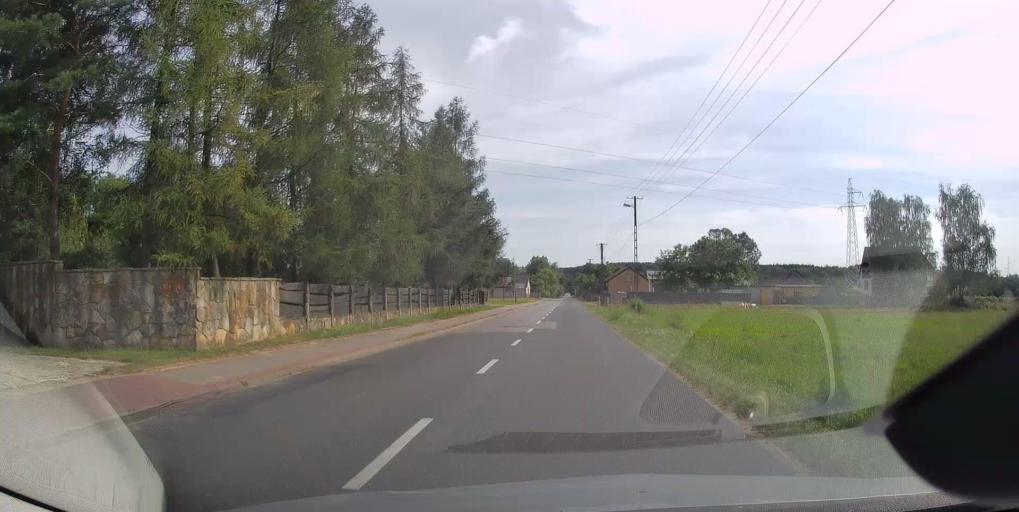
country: PL
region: Lodz Voivodeship
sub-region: Powiat tomaszowski
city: Tomaszow Mazowiecki
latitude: 51.4892
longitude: 19.9888
